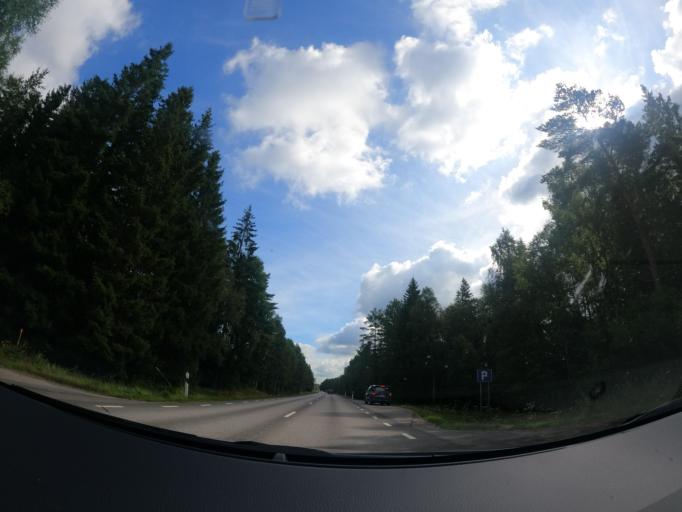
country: SE
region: Halland
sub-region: Hylte Kommun
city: Torup
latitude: 57.1273
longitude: 13.1213
